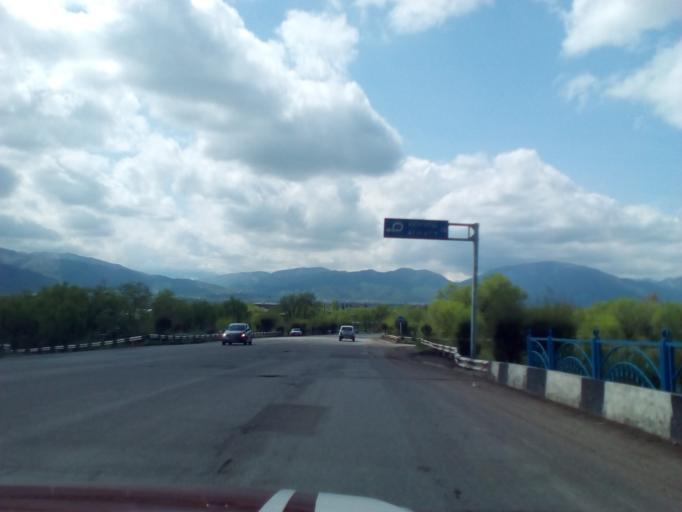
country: KZ
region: Almaty Oblysy
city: Burunday
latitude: 43.2181
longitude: 76.6480
